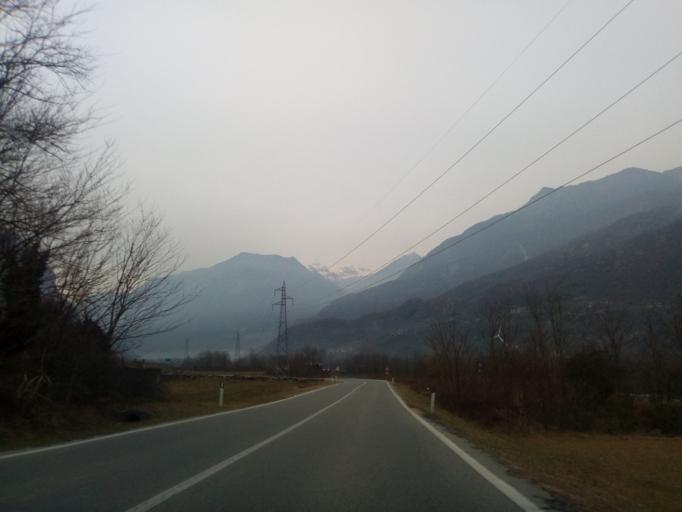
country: IT
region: Piedmont
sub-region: Provincia di Torino
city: Tavagnasco
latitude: 45.5527
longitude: 7.8210
